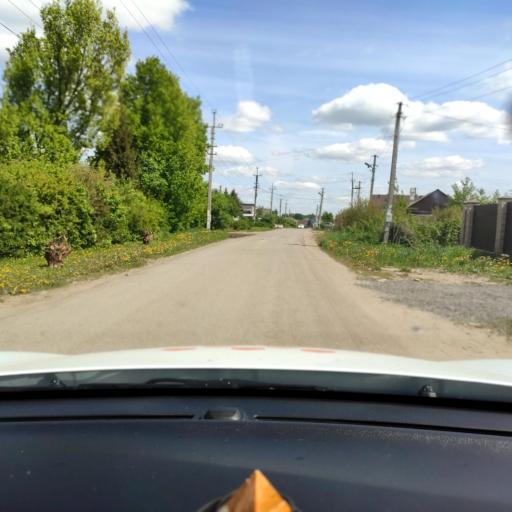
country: RU
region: Tatarstan
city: Osinovo
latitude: 55.8818
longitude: 48.8695
